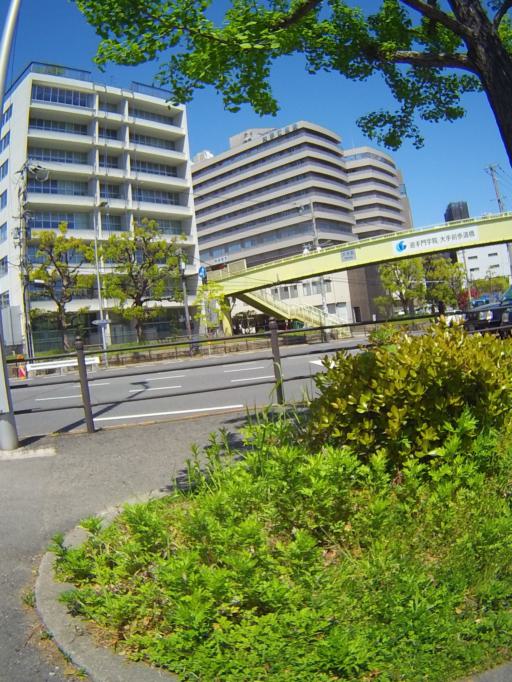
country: JP
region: Osaka
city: Osaka-shi
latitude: 34.6883
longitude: 135.5205
